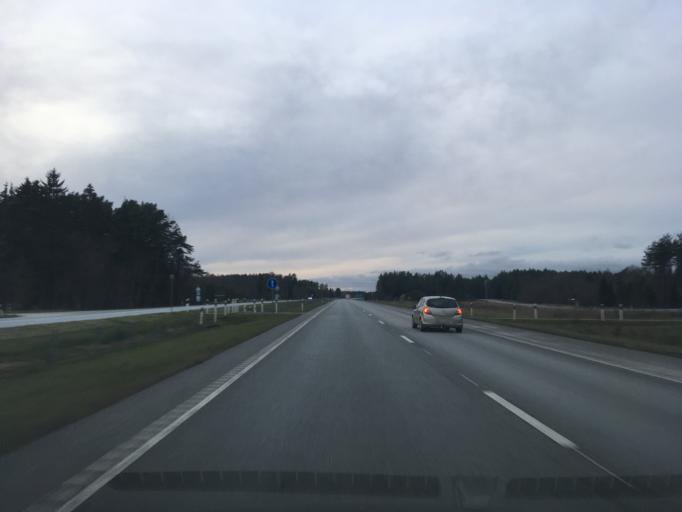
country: EE
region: Laeaene-Virumaa
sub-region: Kadrina vald
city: Kadrina
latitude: 59.4459
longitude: 26.0879
